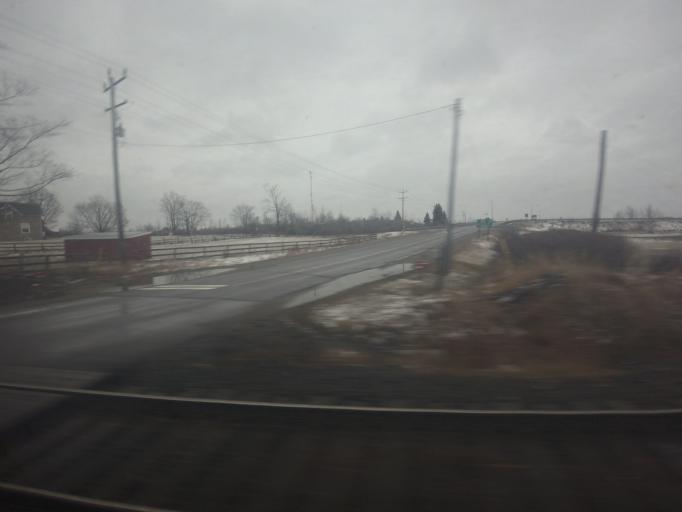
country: CA
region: Ontario
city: Gananoque
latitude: 44.3253
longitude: -76.3312
